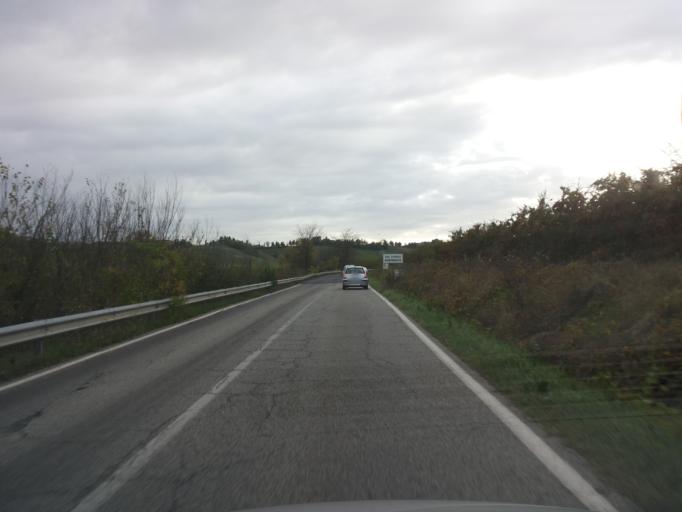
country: IT
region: Piedmont
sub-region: Provincia di Alessandria
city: San Giorgio Monferrato
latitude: 45.1018
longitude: 8.4318
